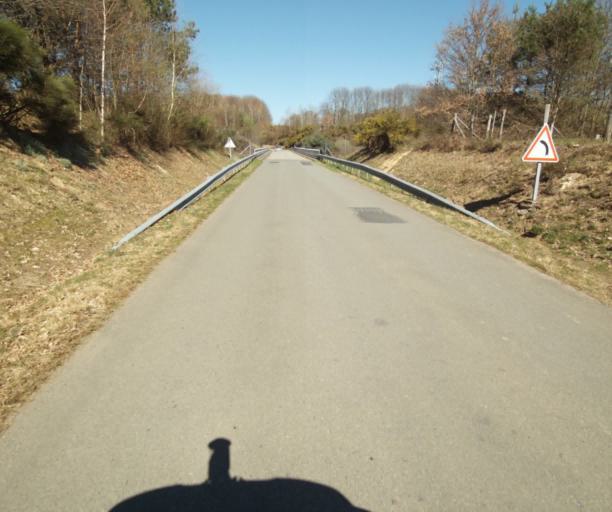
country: FR
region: Limousin
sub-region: Departement de la Correze
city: Saint-Clement
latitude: 45.3070
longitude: 1.6901
